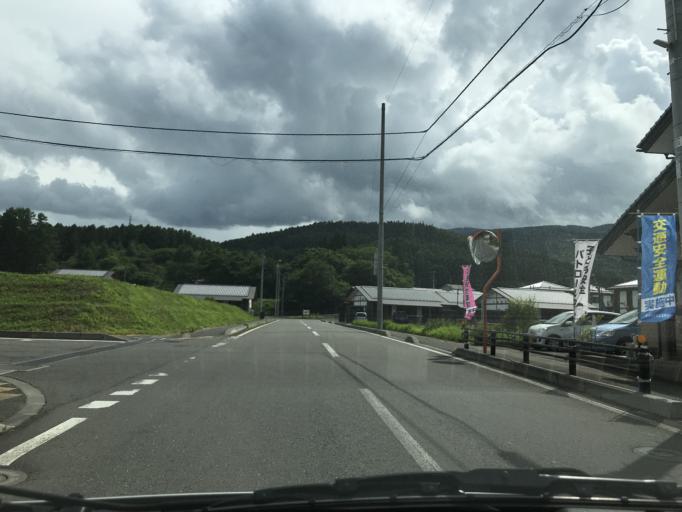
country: JP
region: Iwate
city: Tono
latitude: 39.3246
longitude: 141.5369
